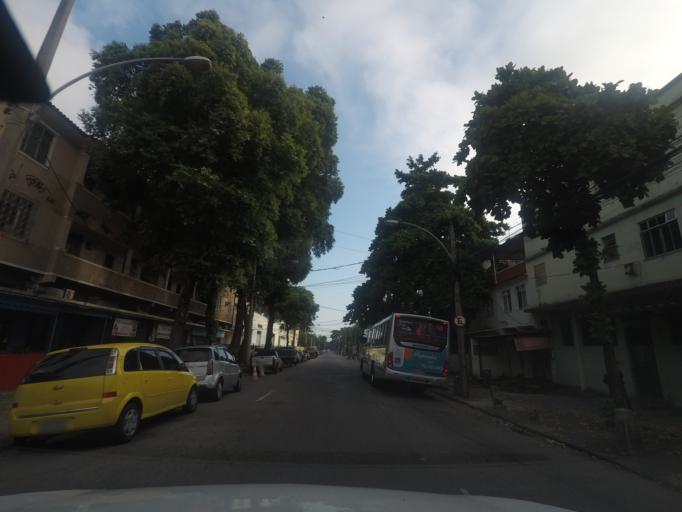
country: BR
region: Rio de Janeiro
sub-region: Duque De Caxias
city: Duque de Caxias
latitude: -22.8316
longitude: -43.2758
